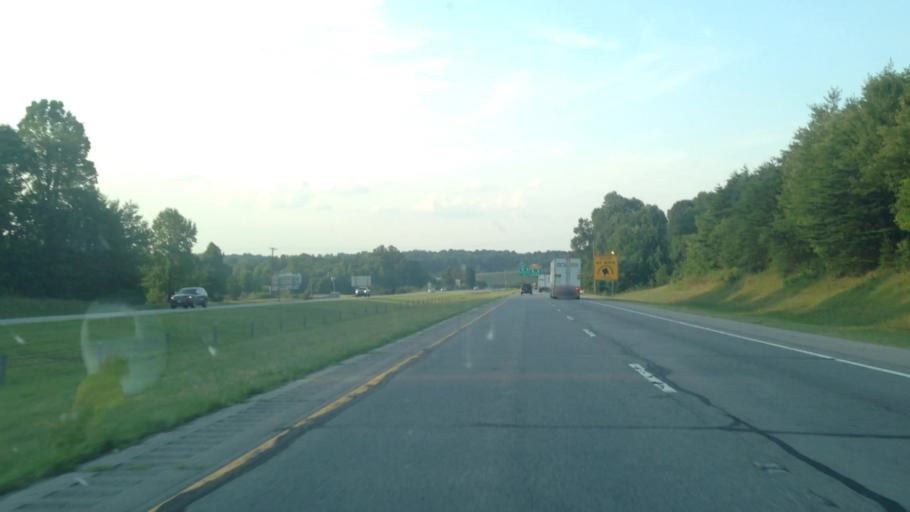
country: US
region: Virginia
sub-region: City of Danville
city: Danville
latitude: 36.5317
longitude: -79.4701
